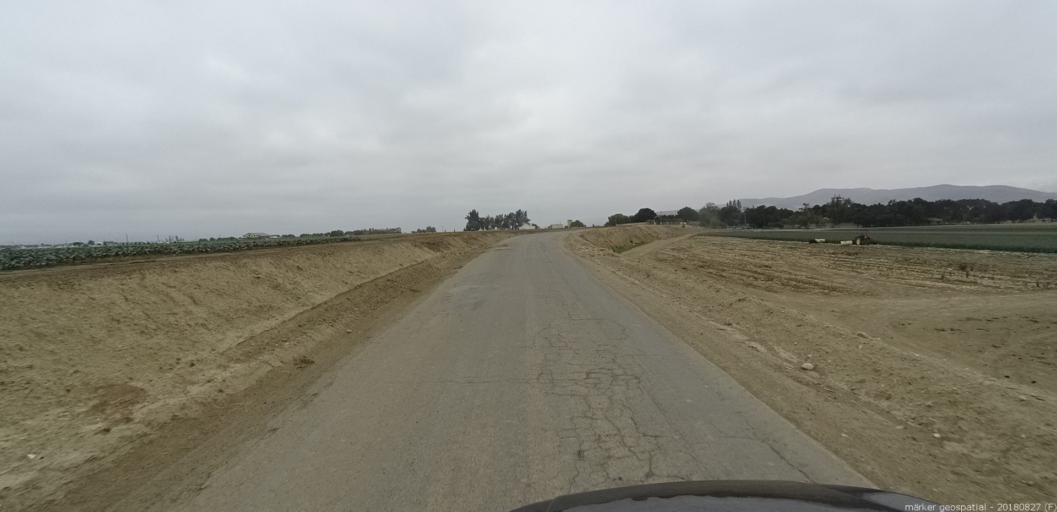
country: US
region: California
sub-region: Monterey County
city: Greenfield
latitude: 36.3304
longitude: -121.2098
